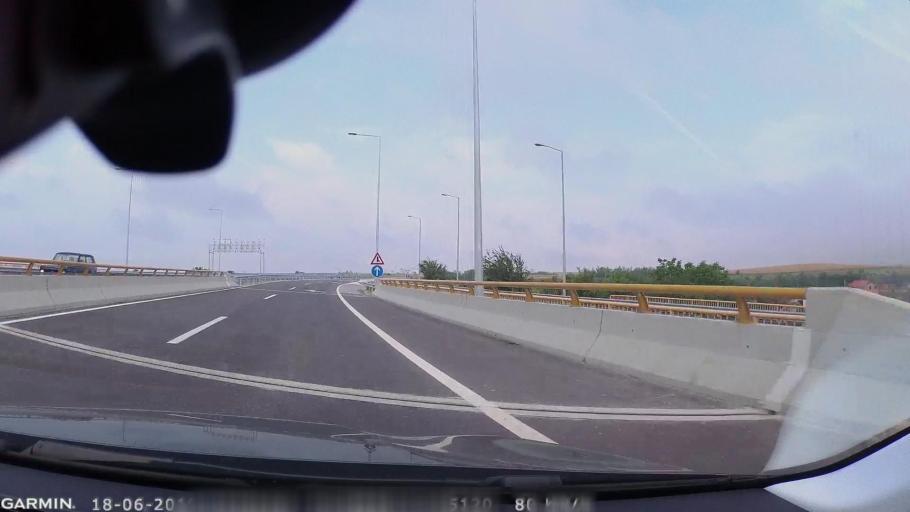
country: MK
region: Petrovec
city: Sredno Konjare
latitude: 41.9522
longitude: 21.7566
